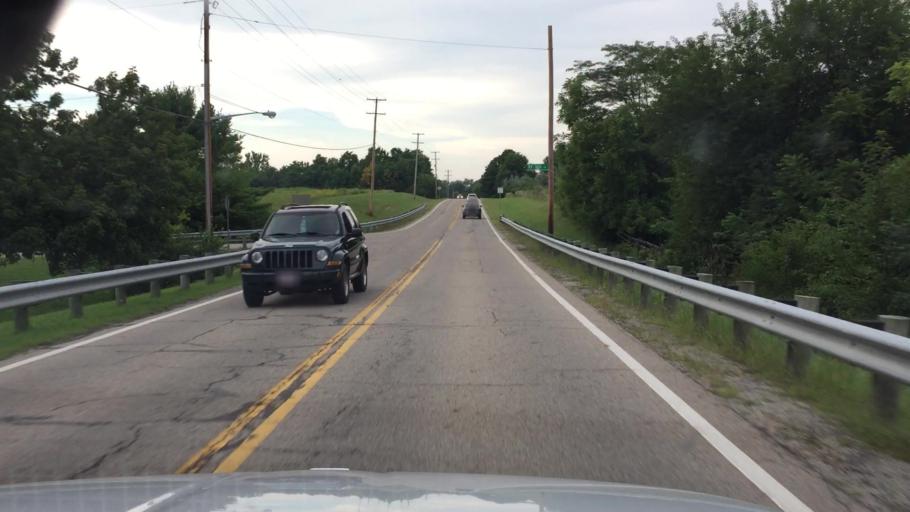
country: US
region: Ohio
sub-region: Franklin County
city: Lake Darby
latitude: 40.0246
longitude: -83.2619
